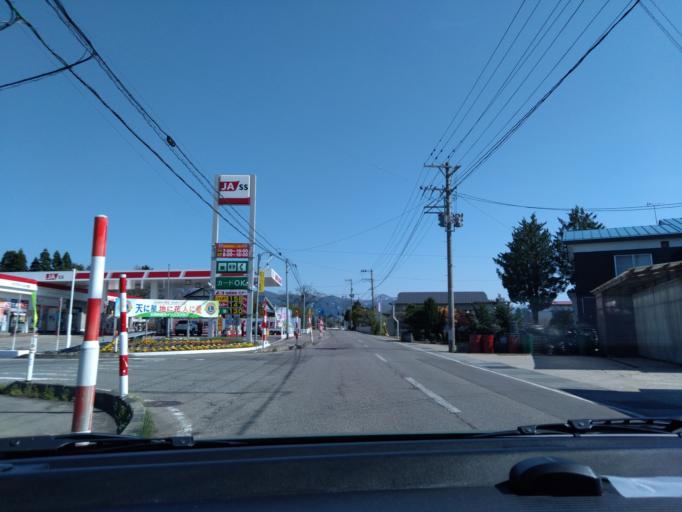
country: JP
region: Akita
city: Kakunodatemachi
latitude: 39.5097
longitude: 140.5943
